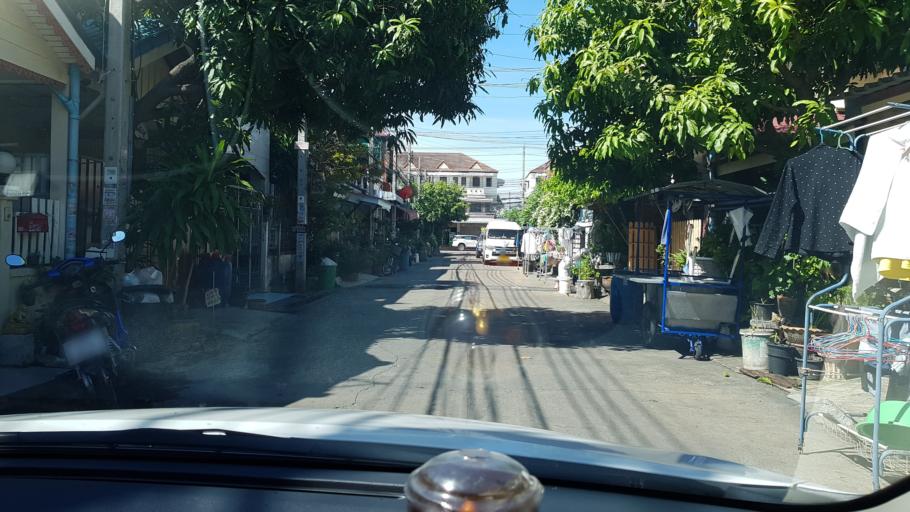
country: TH
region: Bangkok
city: Khlong Sam Wa
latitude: 13.8848
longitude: 100.7161
